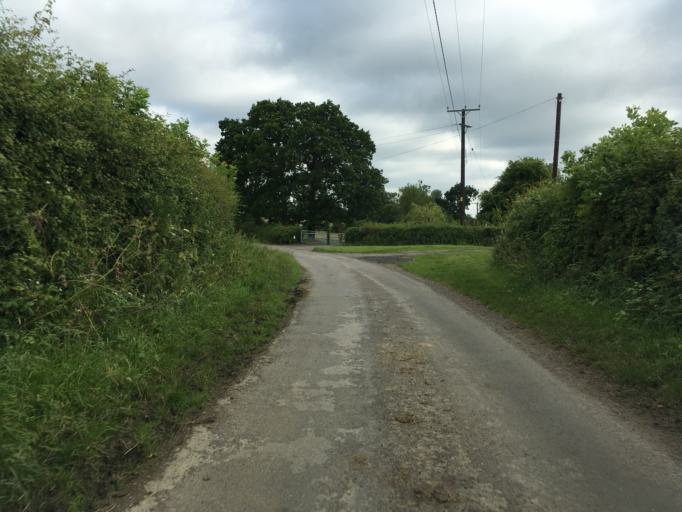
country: GB
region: England
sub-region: South Gloucestershire
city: Horton
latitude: 51.5865
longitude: -2.3470
